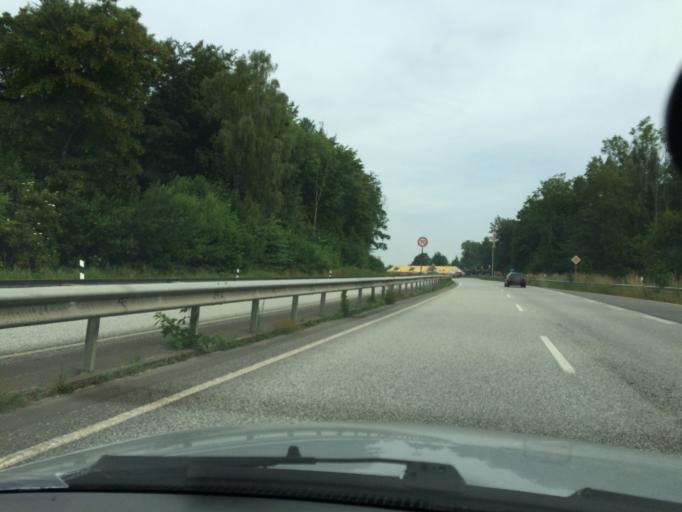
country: DK
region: South Denmark
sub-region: Aabenraa Kommune
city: Krusa
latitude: 54.8321
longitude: 9.4139
